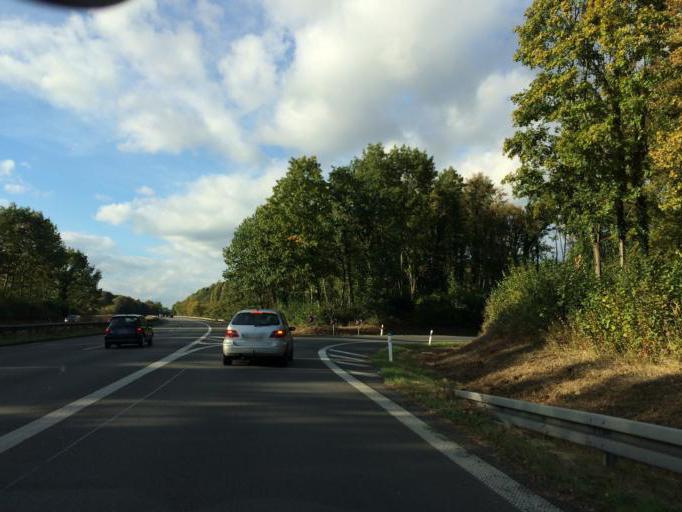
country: DE
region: North Rhine-Westphalia
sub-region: Regierungsbezirk Koln
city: Konigswinter
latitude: 50.7252
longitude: 7.1630
